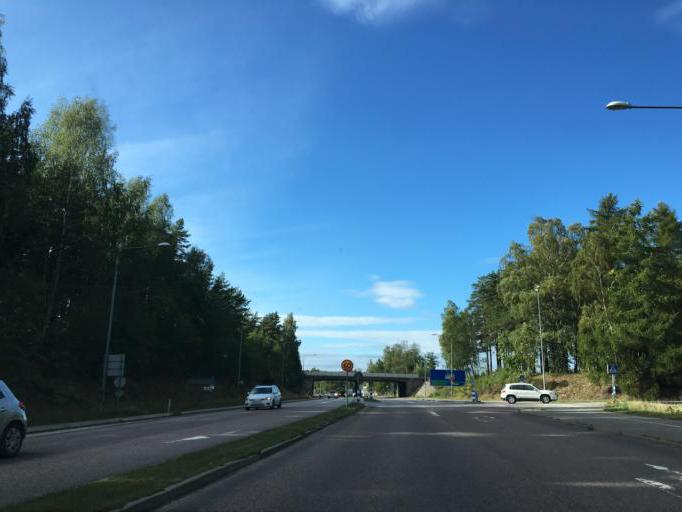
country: SE
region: Soedermanland
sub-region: Nykopings Kommun
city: Nykoping
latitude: 58.7629
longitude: 16.9932
